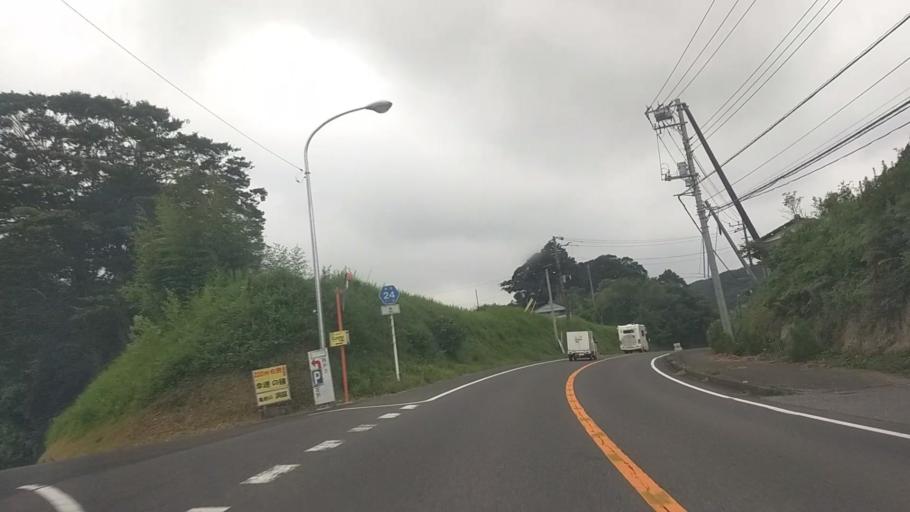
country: JP
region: Chiba
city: Kawaguchi
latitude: 35.1900
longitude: 140.0629
